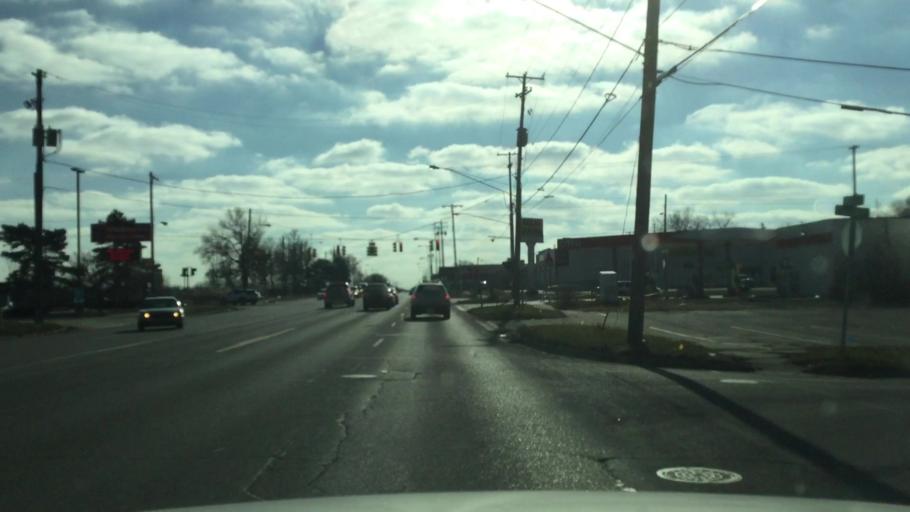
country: US
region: Michigan
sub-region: Genesee County
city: Flint
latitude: 43.0338
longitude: -83.6554
